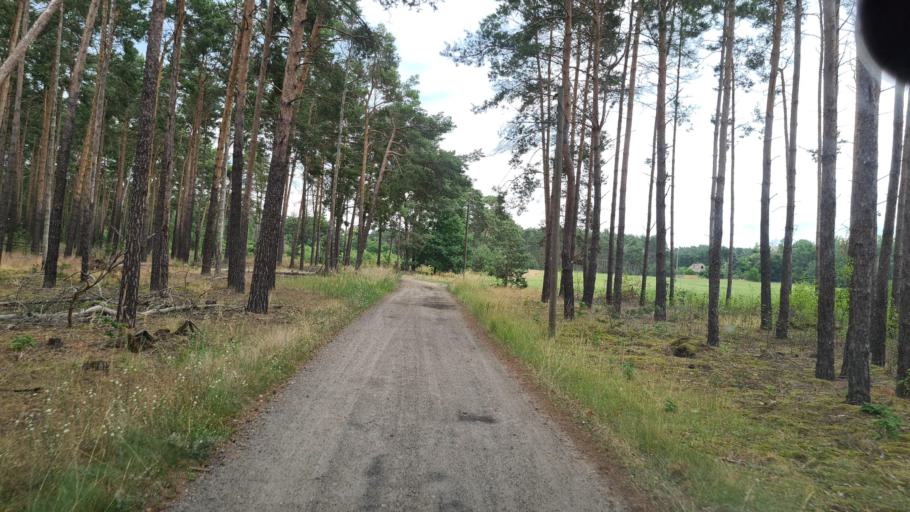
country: DE
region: Brandenburg
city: Crinitz
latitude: 51.6641
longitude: 13.7927
